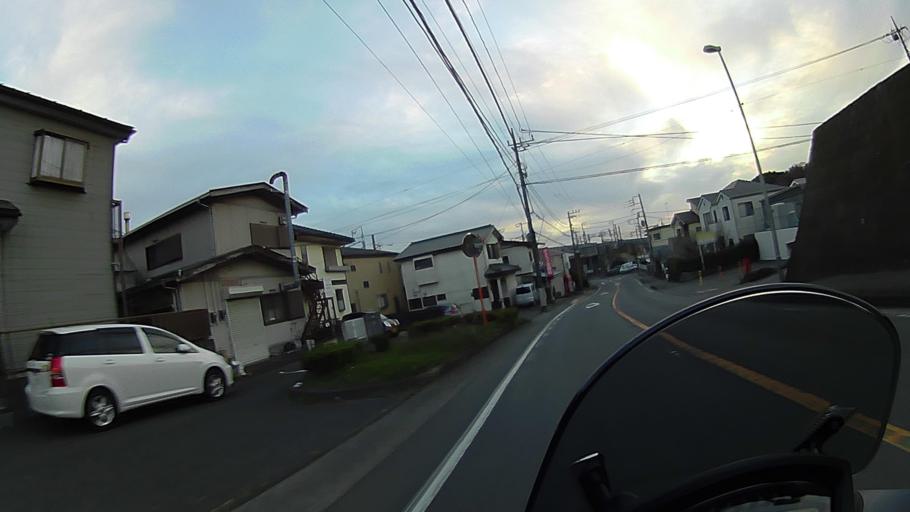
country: JP
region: Kanagawa
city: Atsugi
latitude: 35.4106
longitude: 139.4157
